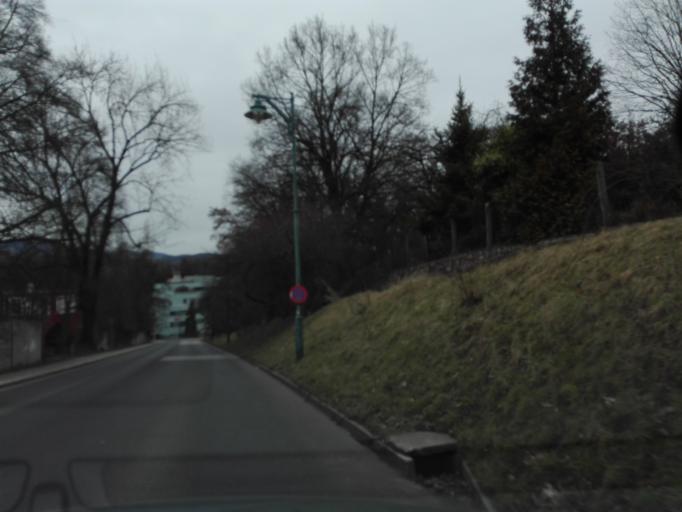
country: AT
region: Upper Austria
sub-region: Linz Stadt
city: Linz
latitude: 48.2965
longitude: 14.2751
